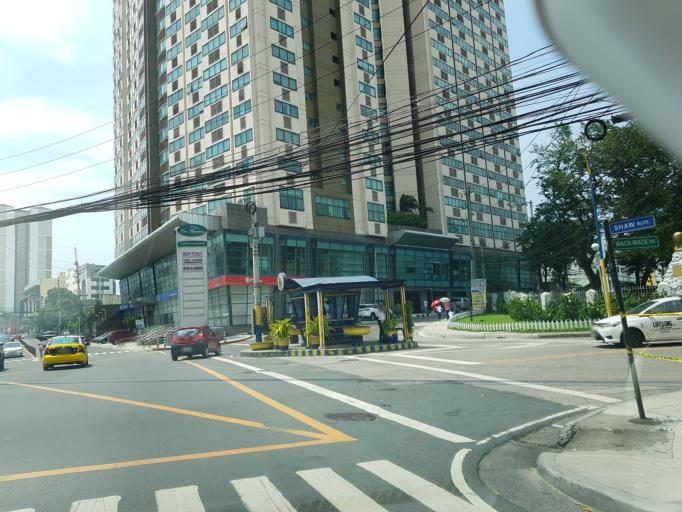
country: PH
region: Metro Manila
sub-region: Mandaluyong
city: Mandaluyong City
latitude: 14.5871
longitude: 121.0466
